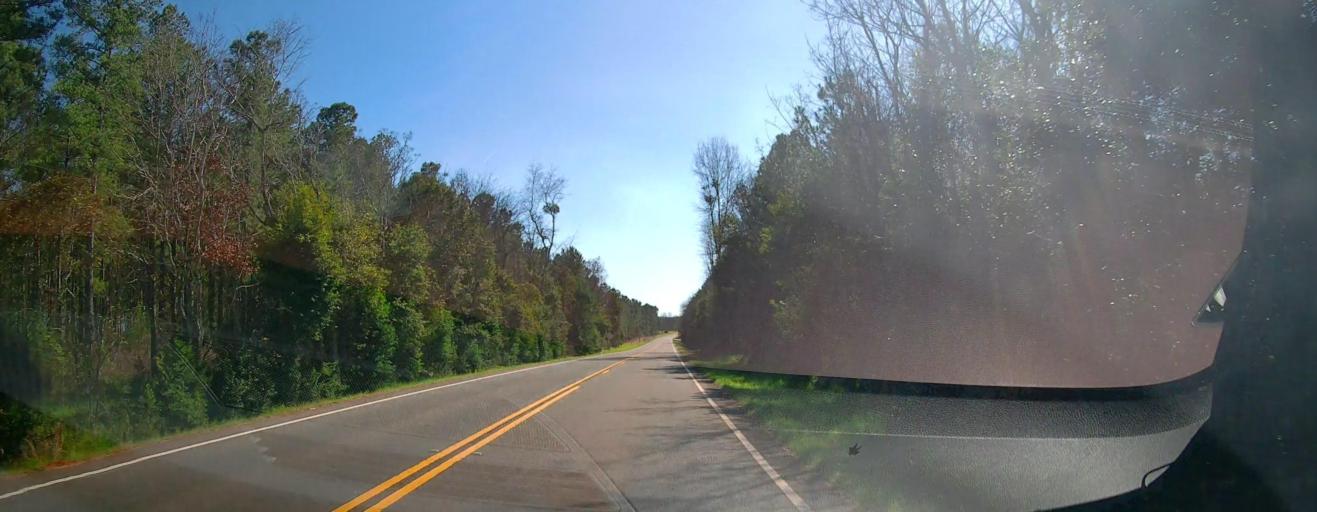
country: US
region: Georgia
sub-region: Macon County
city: Montezuma
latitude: 32.3664
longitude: -84.0132
